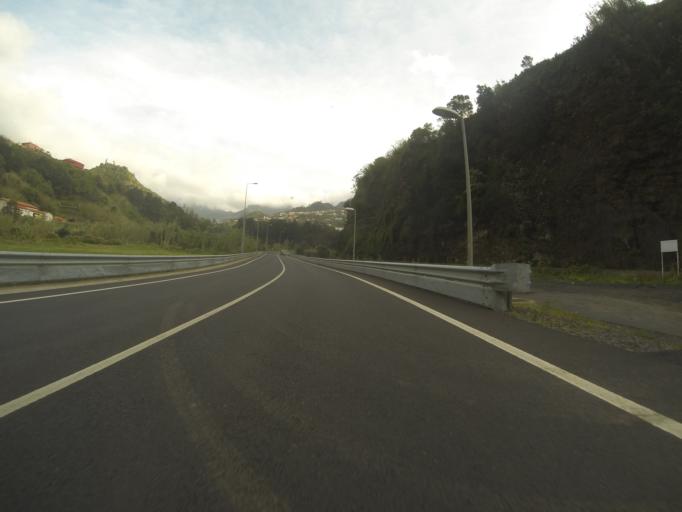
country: PT
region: Madeira
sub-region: Sao Vicente
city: Sao Vicente
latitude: 32.8004
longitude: -17.0434
